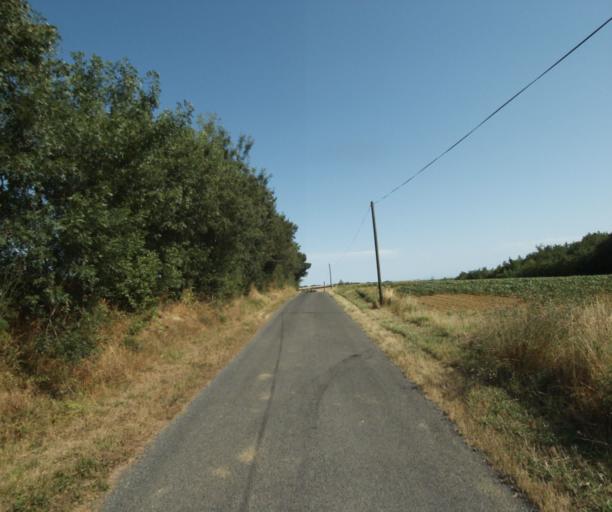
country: FR
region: Midi-Pyrenees
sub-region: Departement de la Haute-Garonne
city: Saint-Felix-Lauragais
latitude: 43.4299
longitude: 1.8514
